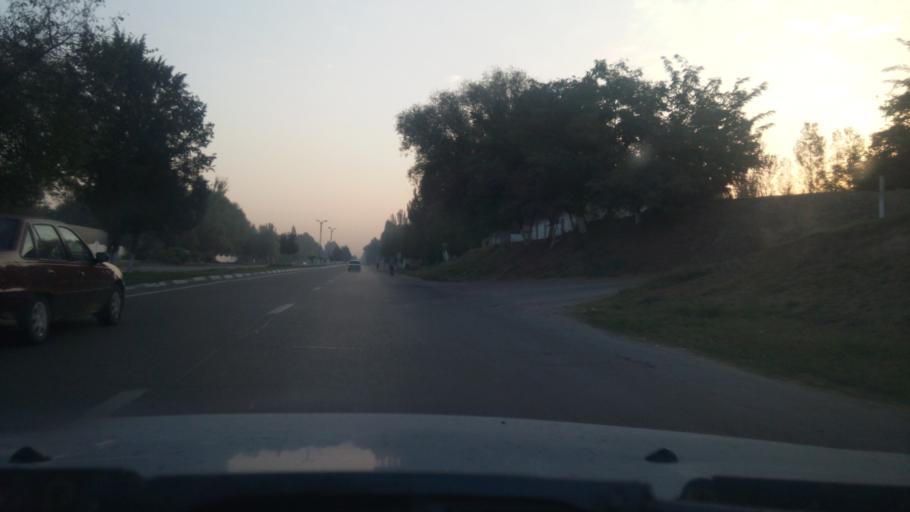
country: UZ
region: Toshkent
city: Amir Timur
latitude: 41.0659
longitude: 68.9175
